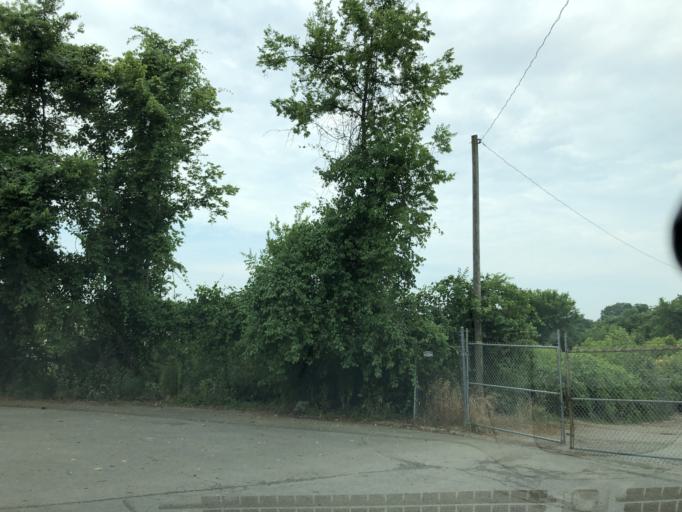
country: US
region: Tennessee
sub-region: Davidson County
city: Oak Hill
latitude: 36.0704
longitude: -86.6821
